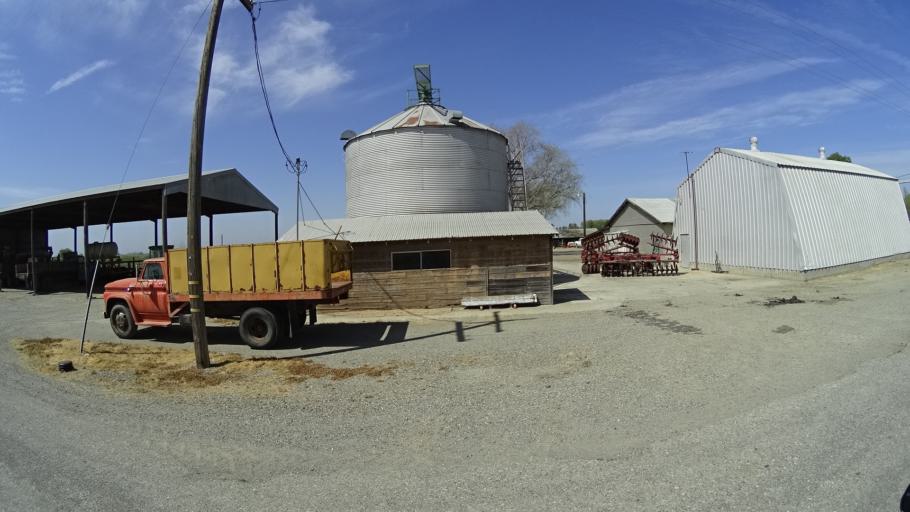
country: US
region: California
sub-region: Glenn County
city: Willows
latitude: 39.5812
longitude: -122.0464
